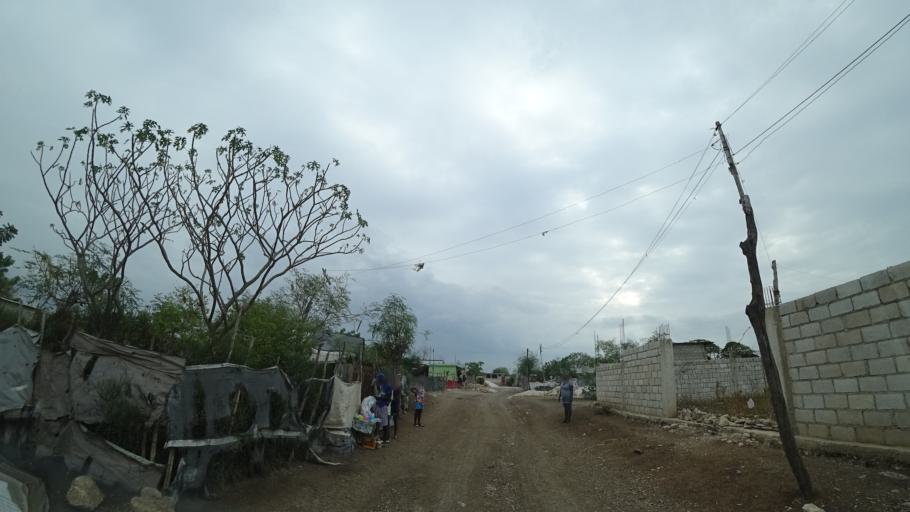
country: HT
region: Ouest
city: Croix des Bouquets
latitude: 18.6490
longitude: -72.2707
